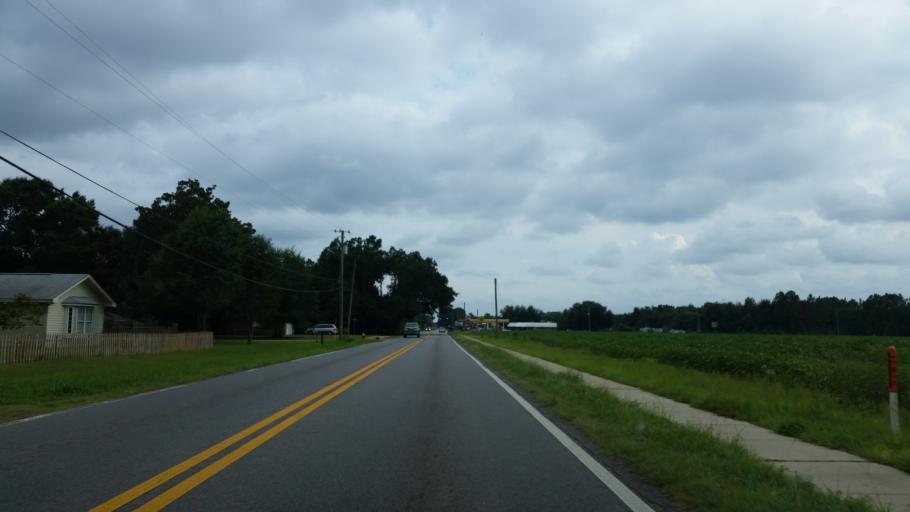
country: US
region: Florida
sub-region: Santa Rosa County
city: Pace
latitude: 30.6174
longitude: -87.1486
